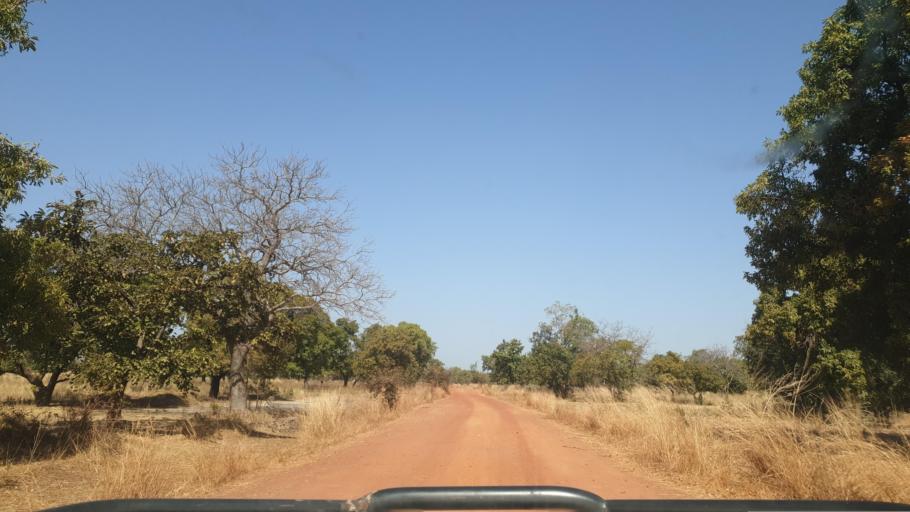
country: ML
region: Koulikoro
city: Dioila
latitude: 11.8988
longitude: -6.9811
